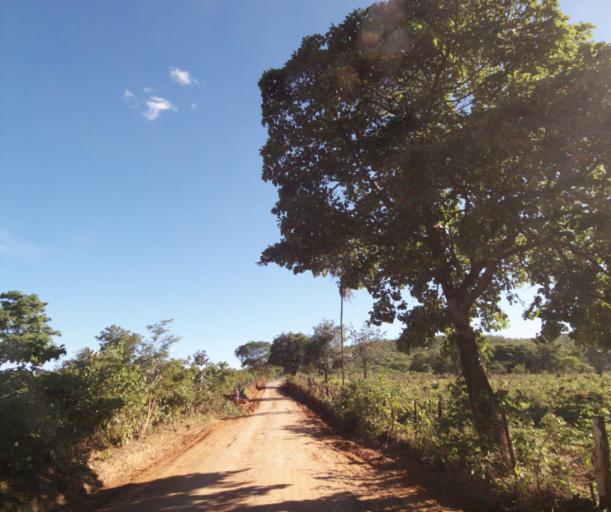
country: BR
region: Bahia
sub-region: Carinhanha
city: Carinhanha
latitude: -14.2914
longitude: -44.4685
